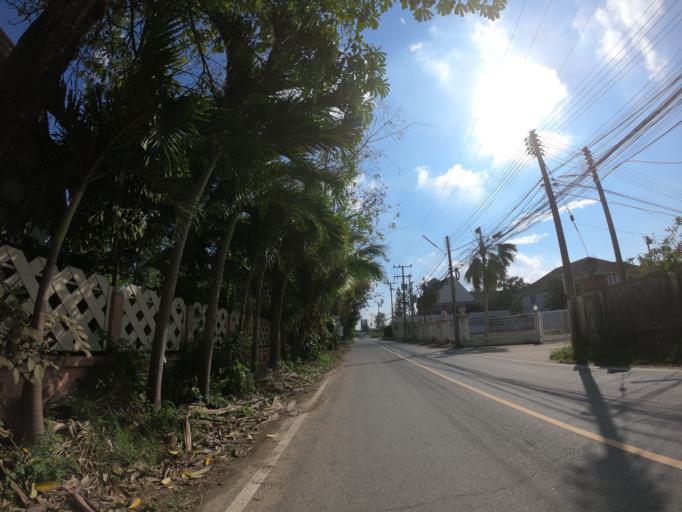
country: TH
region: Chiang Mai
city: San Sai
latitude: 18.8361
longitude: 99.0576
